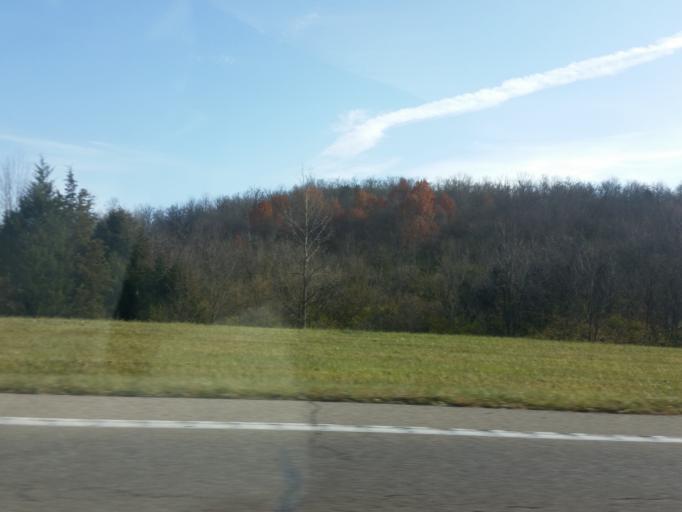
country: US
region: Ohio
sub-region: Butler County
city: Ross
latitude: 39.3478
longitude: -84.6388
